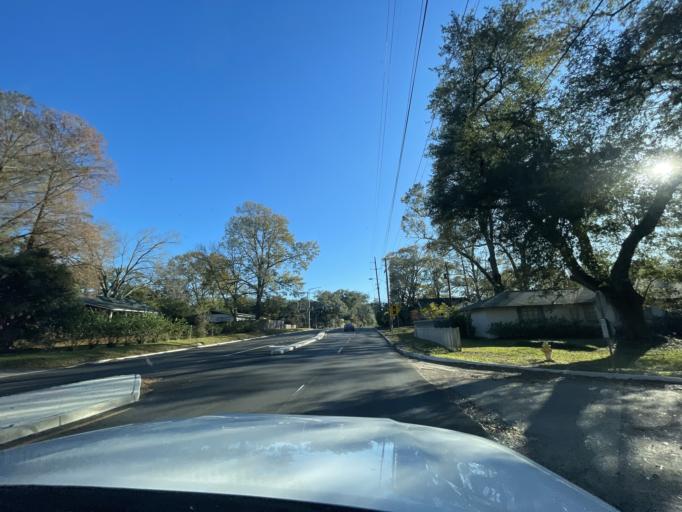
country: US
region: Louisiana
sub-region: East Baton Rouge Parish
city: Baton Rouge
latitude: 30.4333
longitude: -91.1527
